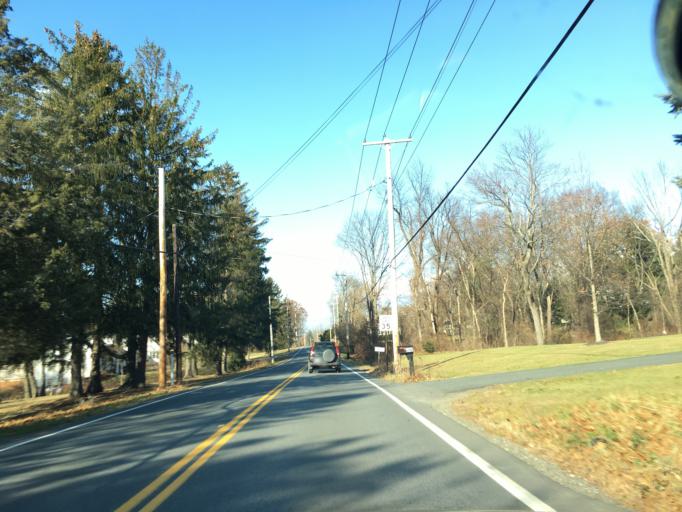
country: US
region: New York
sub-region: Rensselaer County
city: Hampton Manor
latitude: 42.6478
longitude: -73.6871
